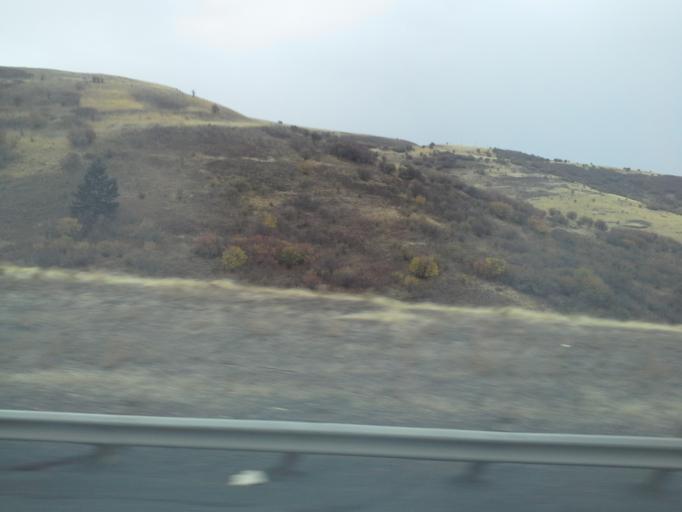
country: US
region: Oregon
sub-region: Umatilla County
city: Mission
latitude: 45.5950
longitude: -118.6120
